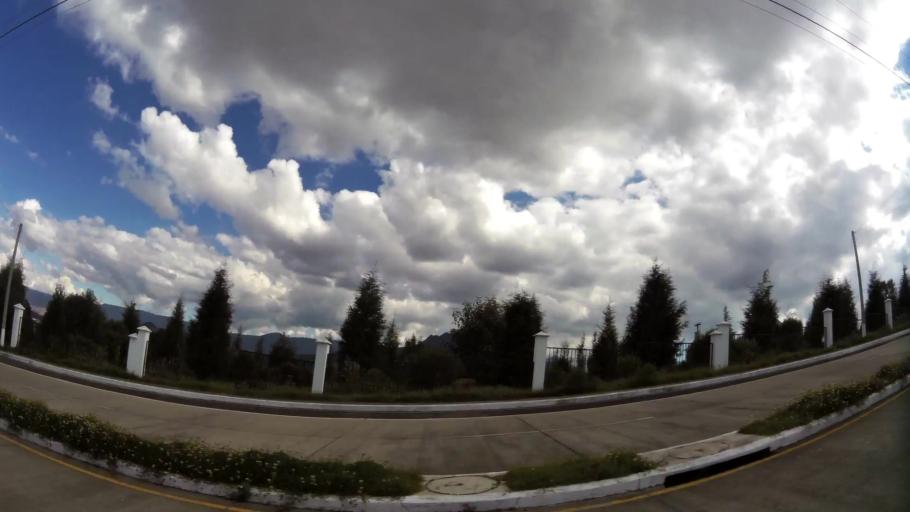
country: GT
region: Quetzaltenango
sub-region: Municipio de La Esperanza
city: La Esperanza
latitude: 14.8365
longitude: -91.5565
